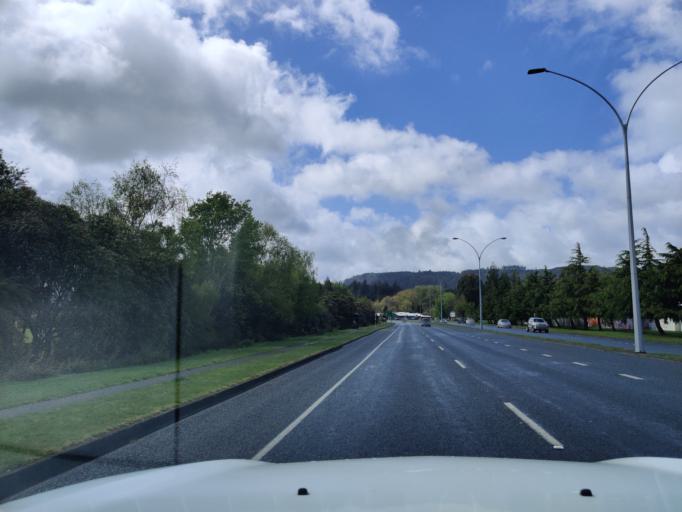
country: NZ
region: Bay of Plenty
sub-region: Rotorua District
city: Rotorua
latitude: -38.1486
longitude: 176.2625
